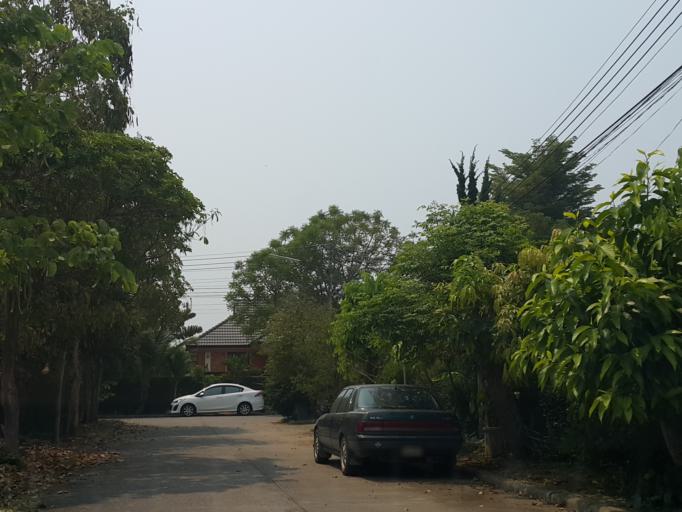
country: TH
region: Chiang Mai
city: Hang Dong
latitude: 18.7266
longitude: 98.9706
